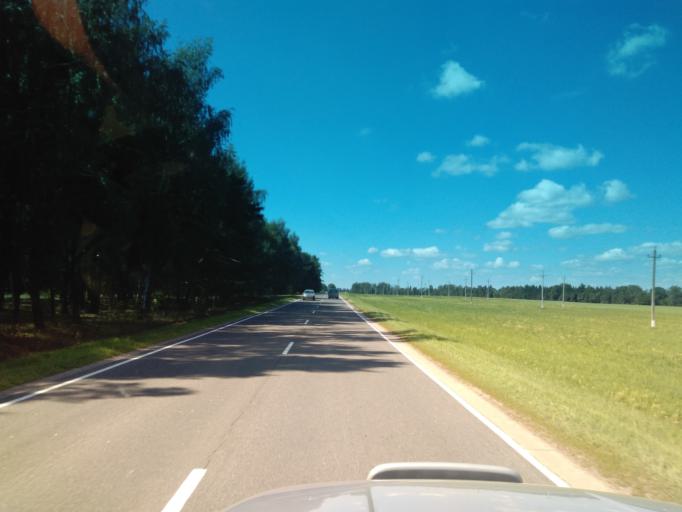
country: BY
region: Minsk
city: Stan'kava
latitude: 53.6250
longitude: 27.2751
